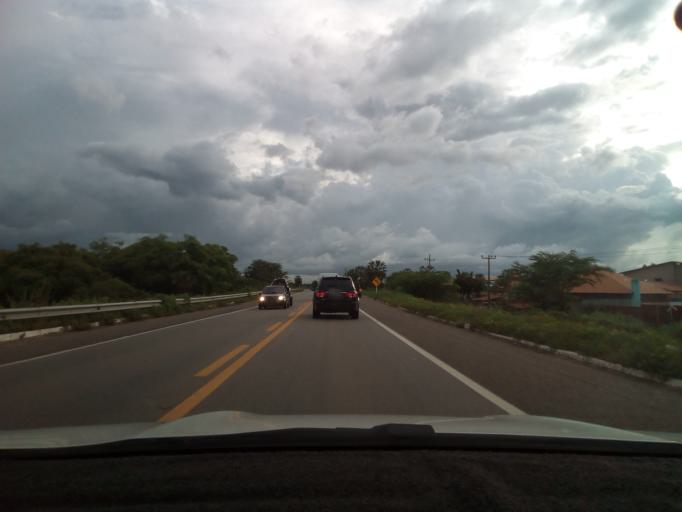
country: BR
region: Ceara
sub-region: Aracati
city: Aracati
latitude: -4.5737
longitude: -37.7625
